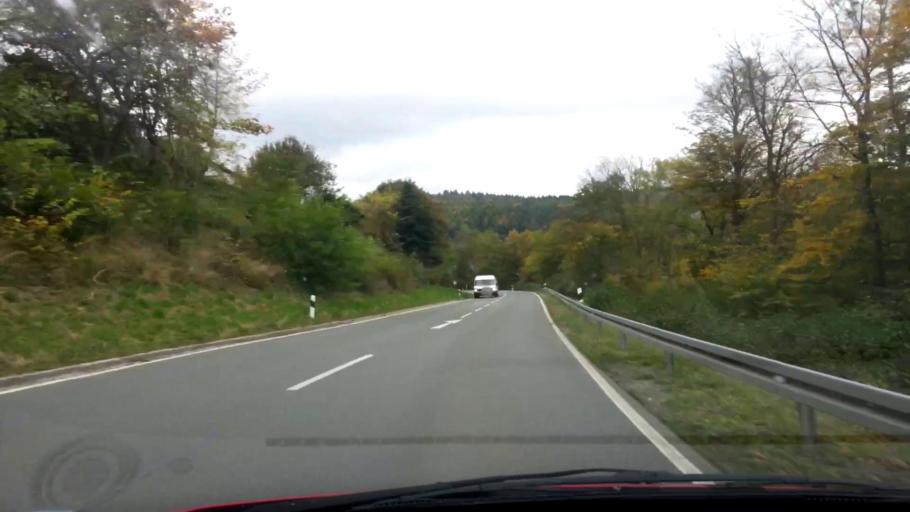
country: DE
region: Bavaria
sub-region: Upper Franconia
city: Kirchenpingarten
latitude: 49.9421
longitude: 11.7499
